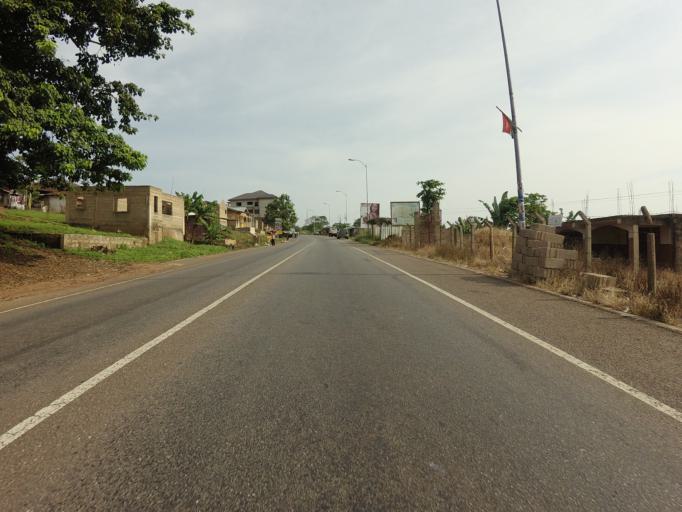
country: GH
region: Eastern
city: Aburi
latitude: 5.8461
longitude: -0.1733
